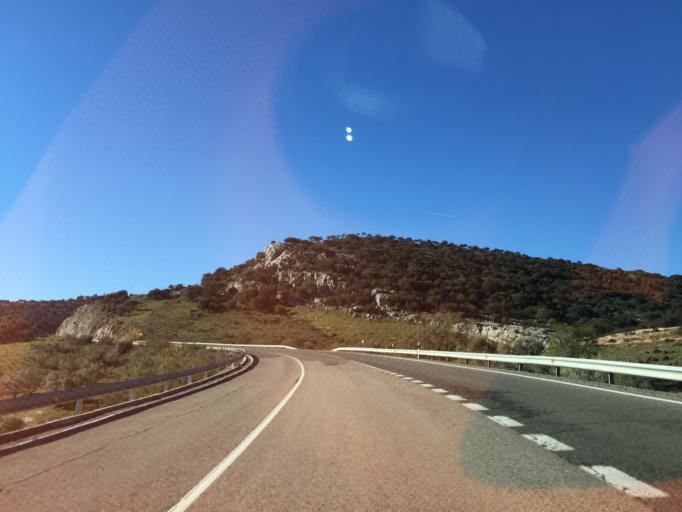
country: ES
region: Andalusia
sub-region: Provincia de Malaga
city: Cuevas del Becerro
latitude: 36.8588
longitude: -5.0623
